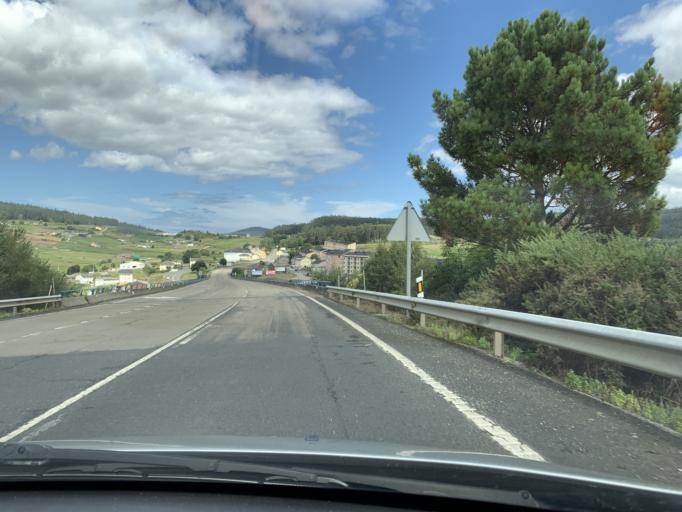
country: ES
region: Galicia
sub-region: Provincia de Lugo
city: Barreiros
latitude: 43.4737
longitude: -7.3031
